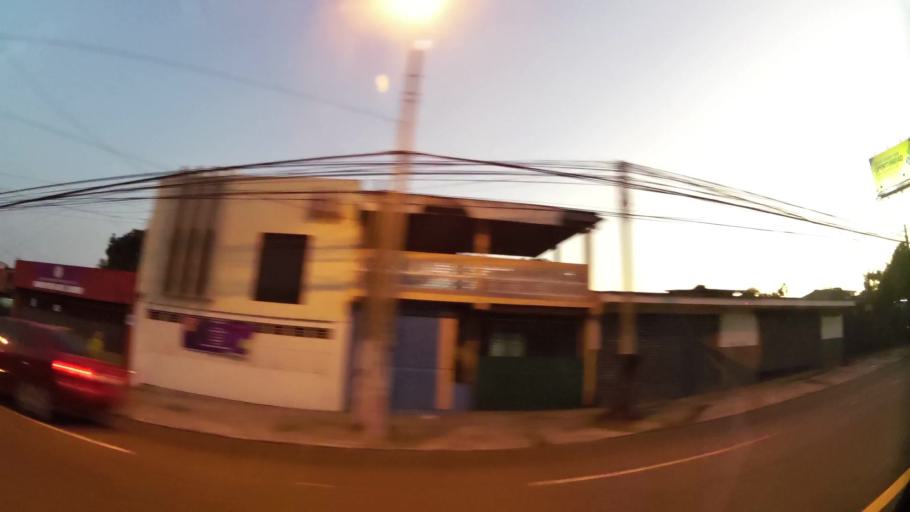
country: SV
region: La Libertad
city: Antiguo Cuscatlan
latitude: 13.6783
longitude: -89.2615
